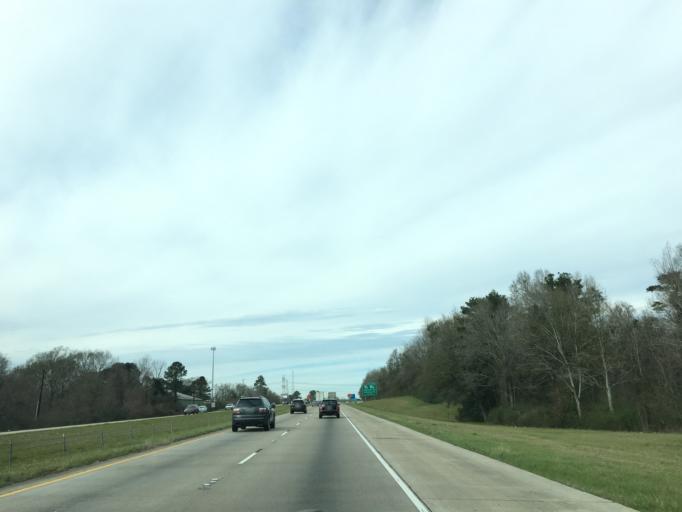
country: US
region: Louisiana
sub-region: East Baton Rouge Parish
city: Old Jefferson
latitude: 30.3367
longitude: -91.0205
